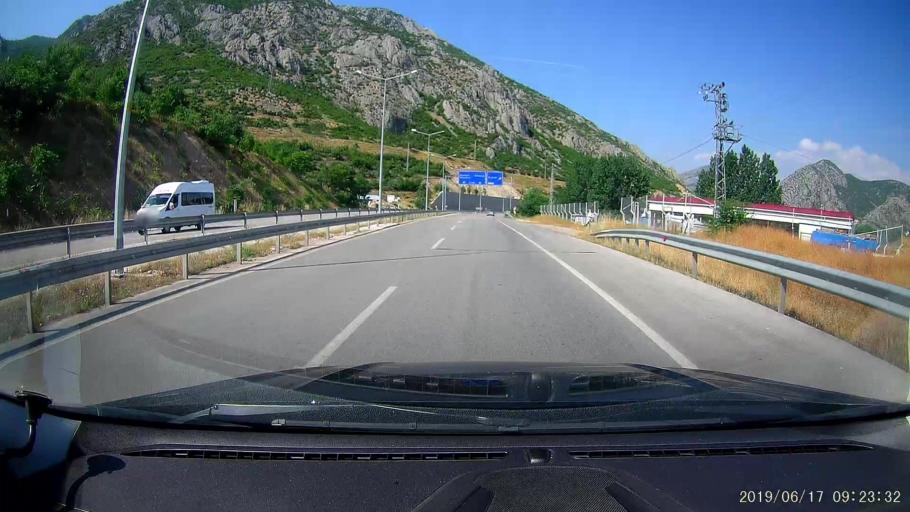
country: TR
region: Amasya
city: Amasya
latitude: 40.6752
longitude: 35.8722
